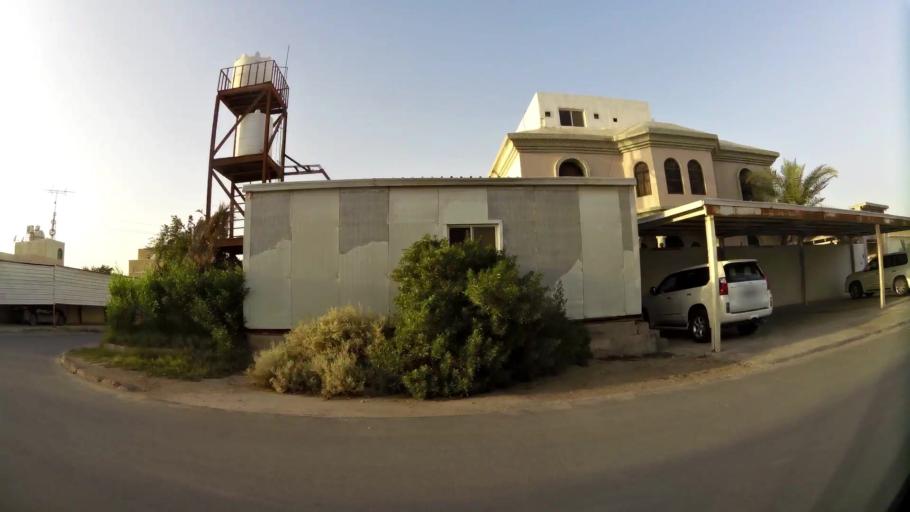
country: QA
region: Baladiyat ar Rayyan
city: Ar Rayyan
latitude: 25.3168
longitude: 51.4566
